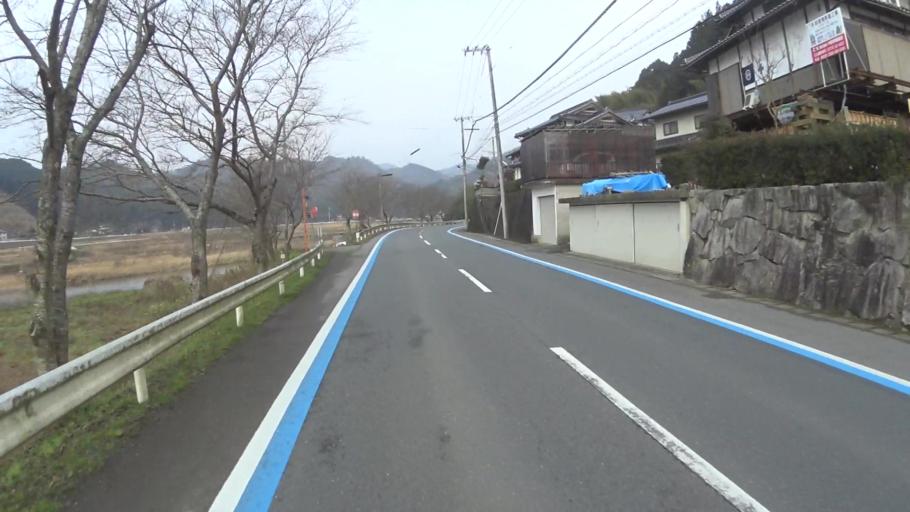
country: JP
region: Kyoto
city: Ayabe
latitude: 35.4000
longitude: 135.1870
